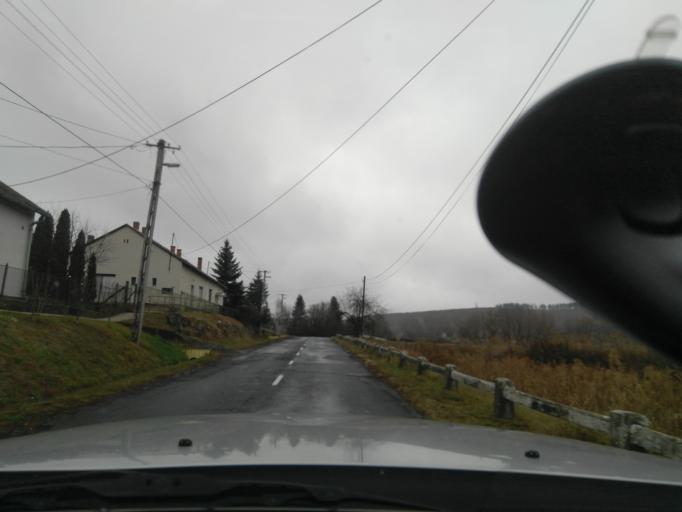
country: HU
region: Nograd
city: Kazar
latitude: 48.0258
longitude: 19.8687
